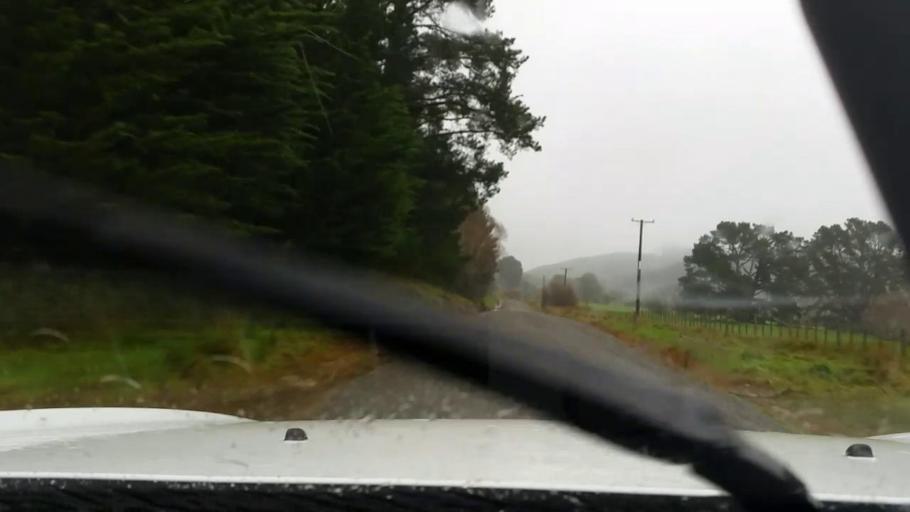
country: NZ
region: Wellington
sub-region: Masterton District
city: Masterton
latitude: -41.1793
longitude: 175.8303
